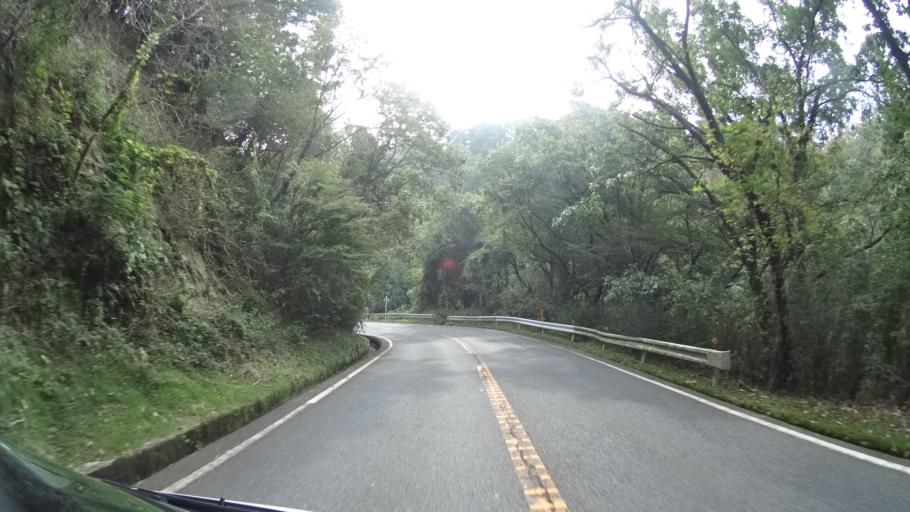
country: JP
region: Shiga Prefecture
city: Otsu-shi
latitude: 35.0404
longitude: 135.8245
